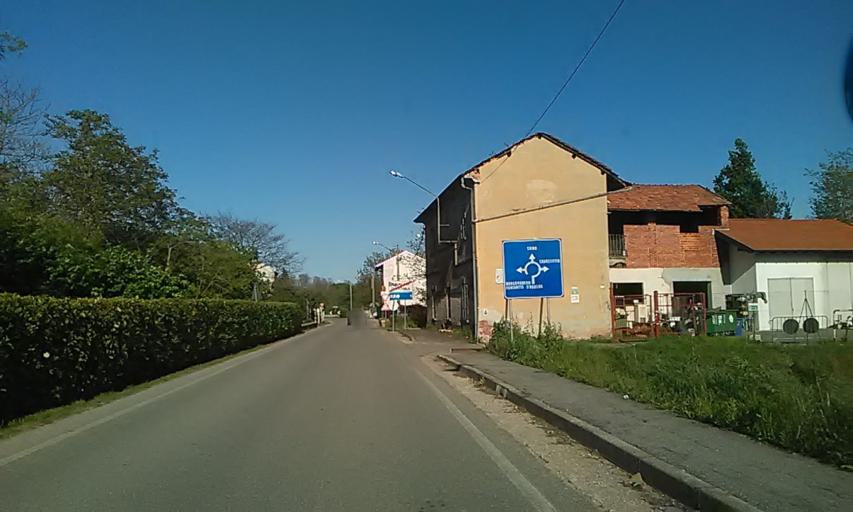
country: IT
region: Piedmont
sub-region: Provincia di Novara
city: Cavaglio D'Agogna
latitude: 45.6120
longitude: 8.4920
